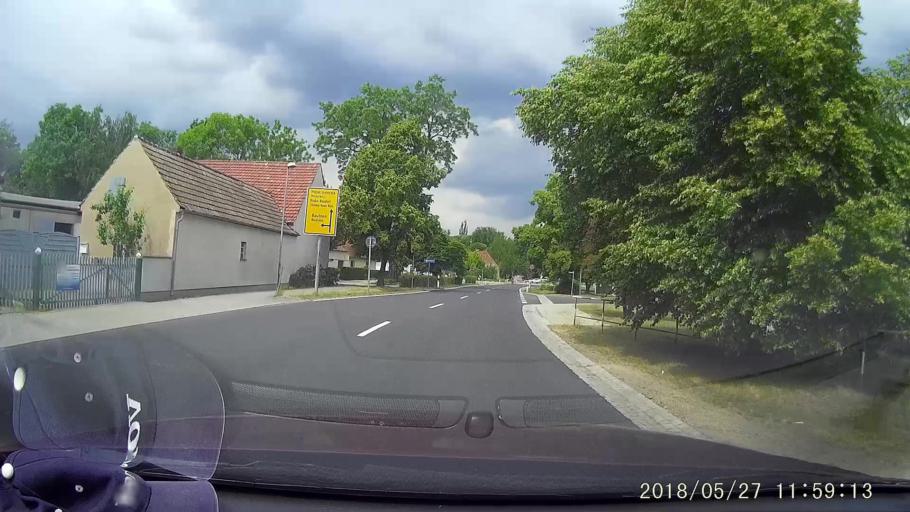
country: DE
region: Saxony
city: Mucka
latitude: 51.3156
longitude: 14.7025
